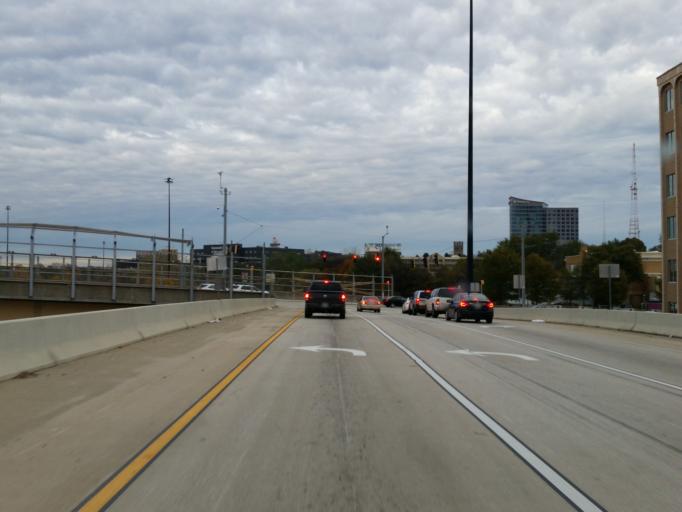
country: US
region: Georgia
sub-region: Fulton County
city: Atlanta
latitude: 33.7910
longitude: -84.3906
